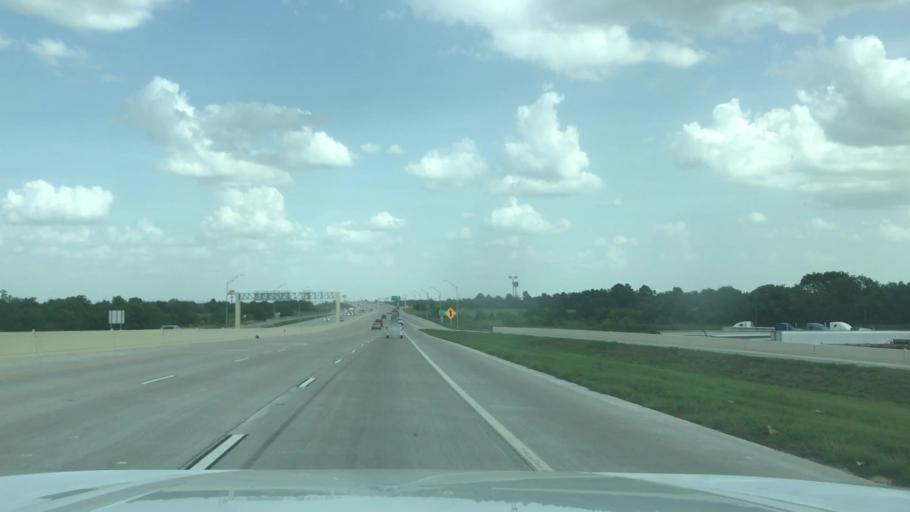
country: US
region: Texas
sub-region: Waller County
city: Waller
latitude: 30.0680
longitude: -95.9195
